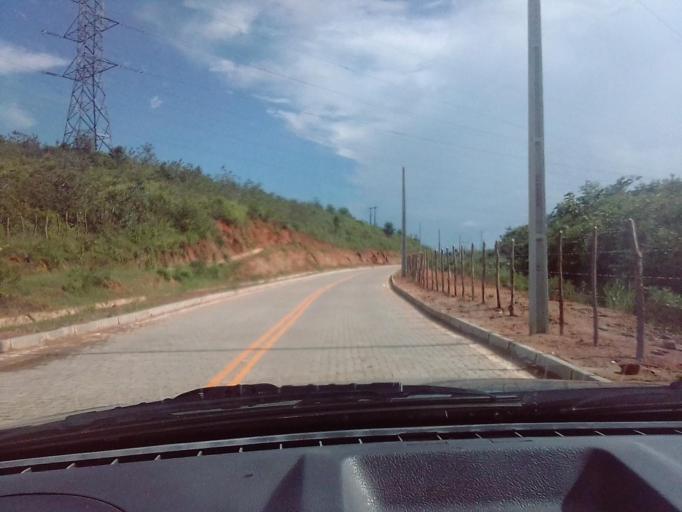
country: BR
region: Pernambuco
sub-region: Jaboatao Dos Guararapes
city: Jaboatao dos Guararapes
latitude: -8.1076
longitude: -35.0325
